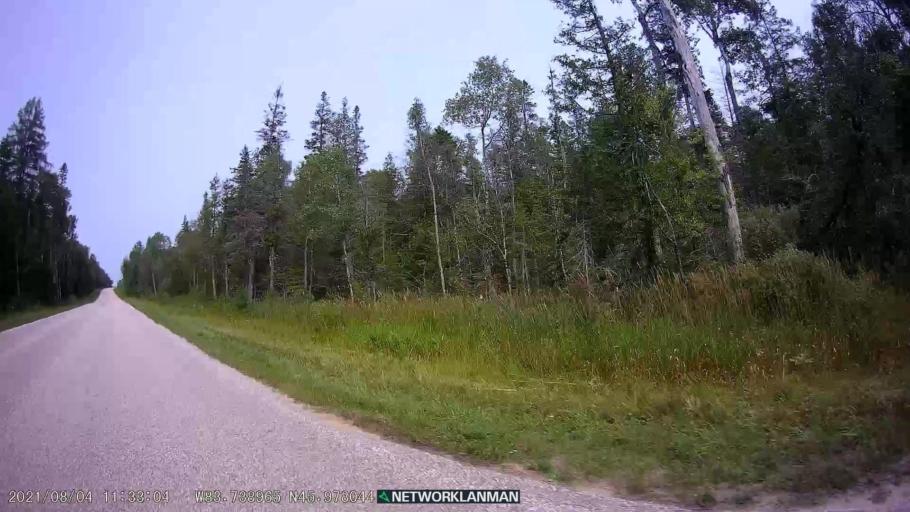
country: CA
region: Ontario
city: Thessalon
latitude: 45.9787
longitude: -83.7389
